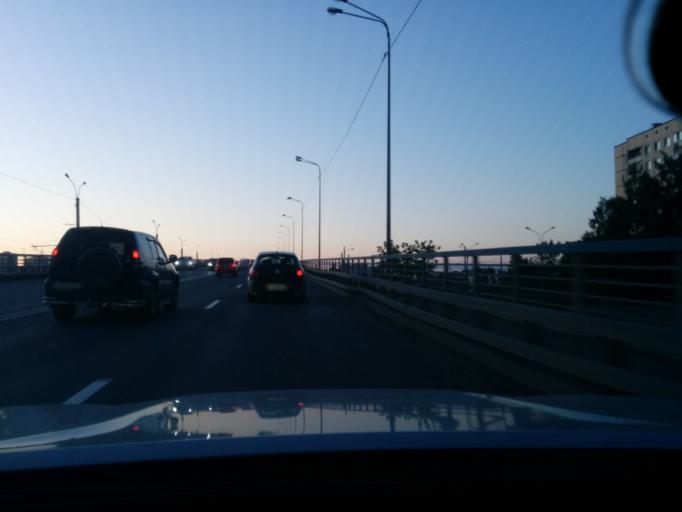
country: RU
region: Leningrad
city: Parnas
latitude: 60.0586
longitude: 30.3396
